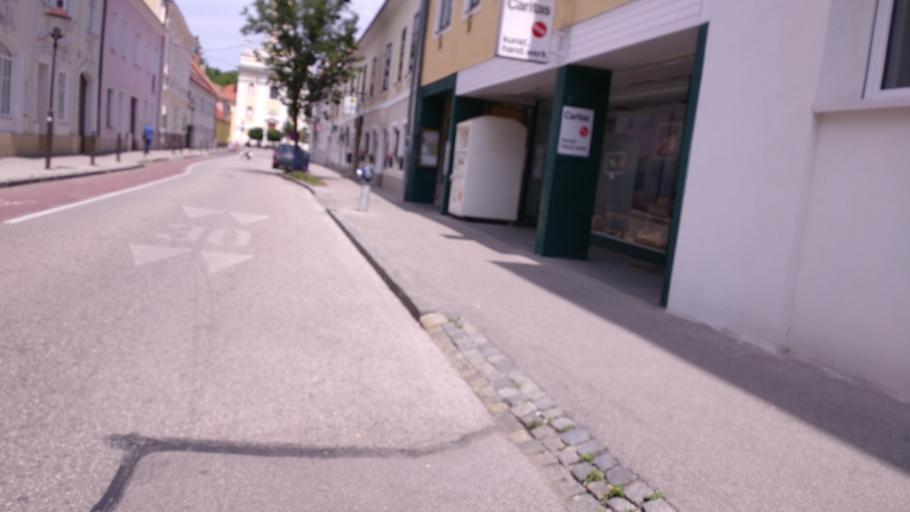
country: AT
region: Lower Austria
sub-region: Wiener Neustadt Stadt
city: Wiener Neustadt
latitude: 47.8174
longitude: 16.2451
